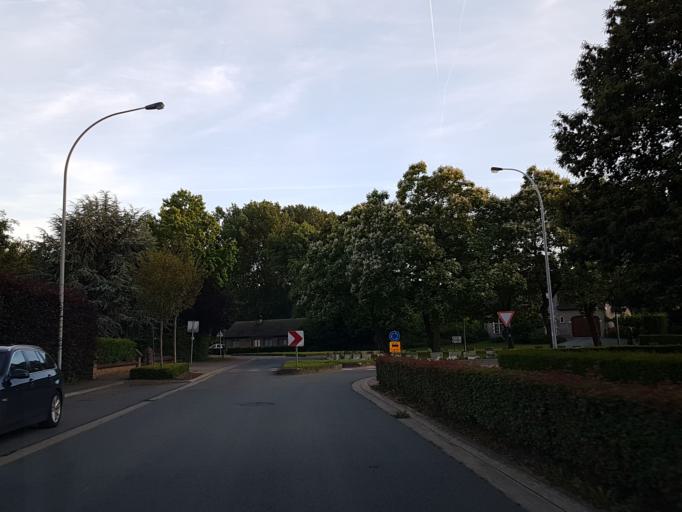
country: BE
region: Flanders
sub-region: Provincie Vlaams-Brabant
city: Londerzeel
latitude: 50.9895
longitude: 4.2652
